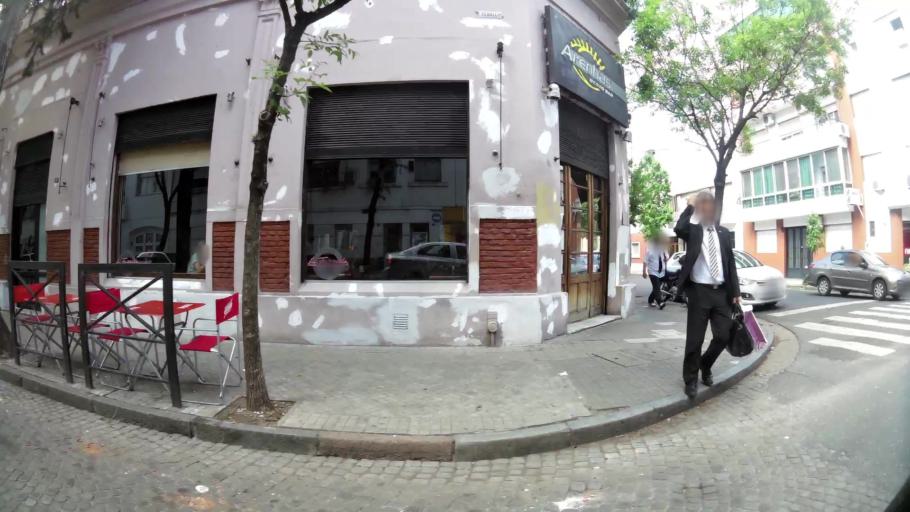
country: AR
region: Santa Fe
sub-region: Departamento de Rosario
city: Rosario
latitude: -32.9561
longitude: -60.6349
